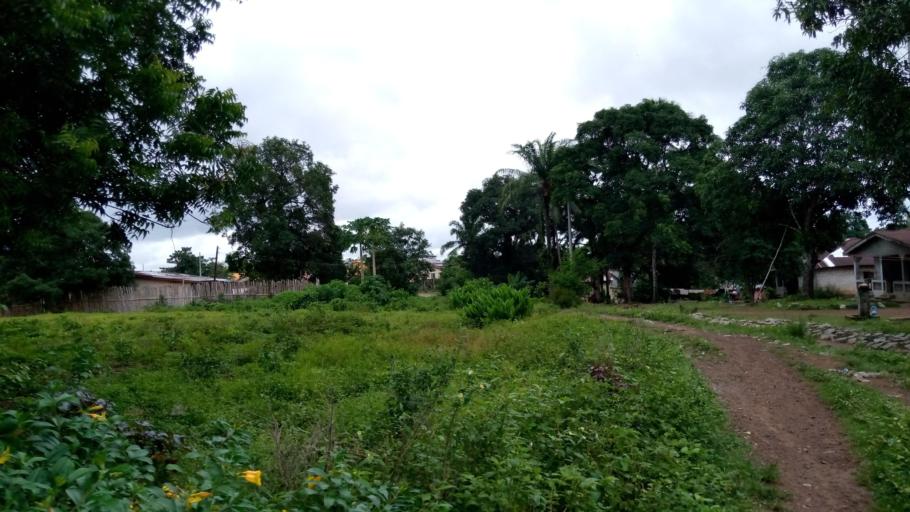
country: SL
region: Southern Province
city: Moyamba
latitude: 8.1598
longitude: -12.4364
